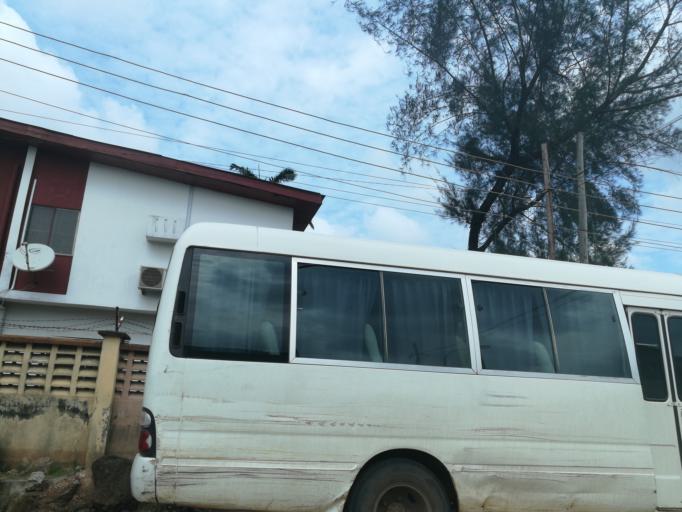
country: NG
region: Lagos
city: Somolu
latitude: 6.5462
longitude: 3.3833
